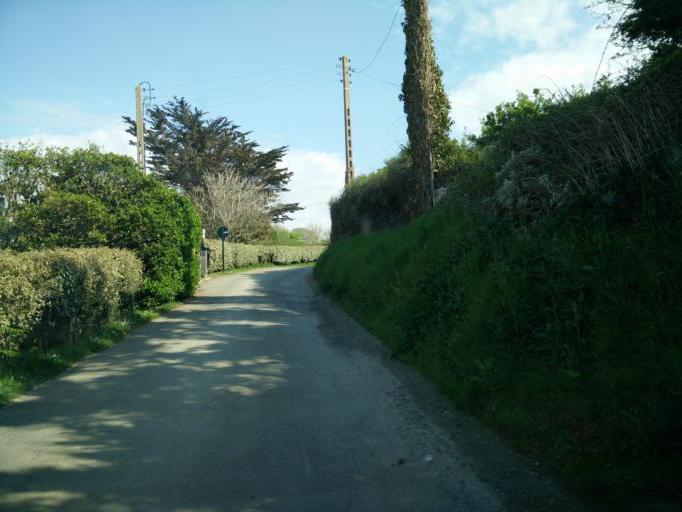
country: FR
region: Brittany
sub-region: Departement du Finistere
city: Crozon
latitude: 48.2401
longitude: -4.5456
